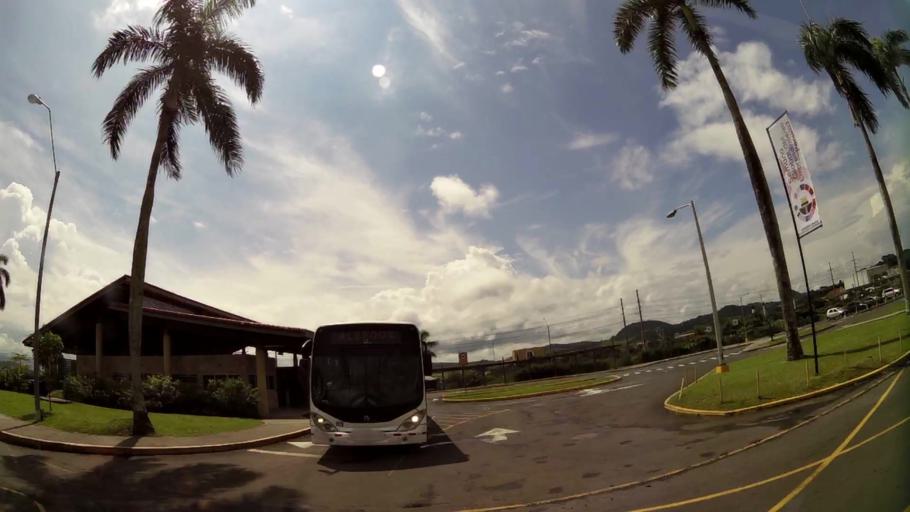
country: PA
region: Panama
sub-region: Distrito de Panama
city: Ancon
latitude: 9.0000
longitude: -79.5852
